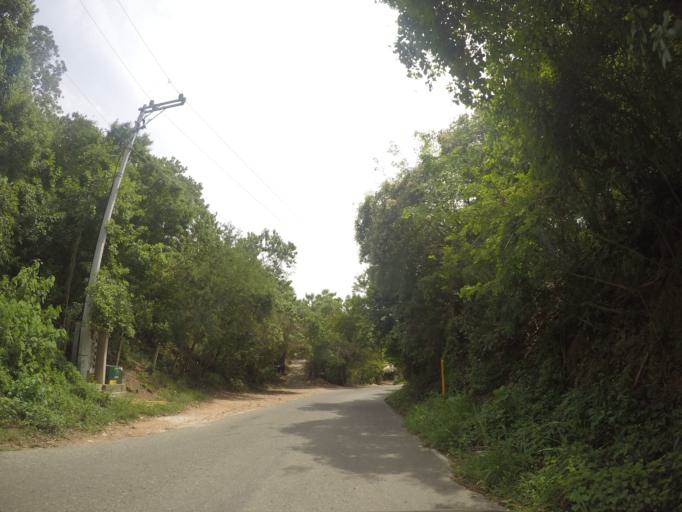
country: MX
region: Oaxaca
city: Santa Maria Tonameca
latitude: 15.6667
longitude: -96.5350
